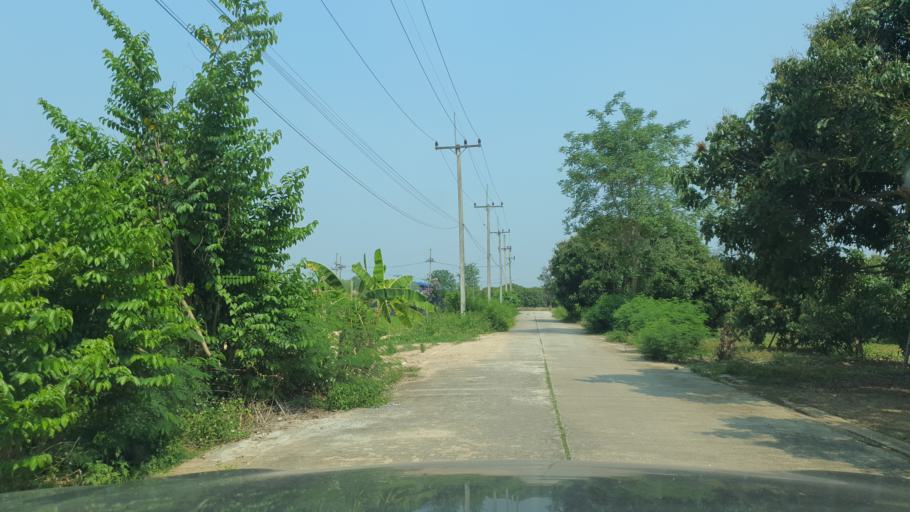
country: TH
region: Chiang Mai
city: Saraphi
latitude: 18.6705
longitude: 98.9884
